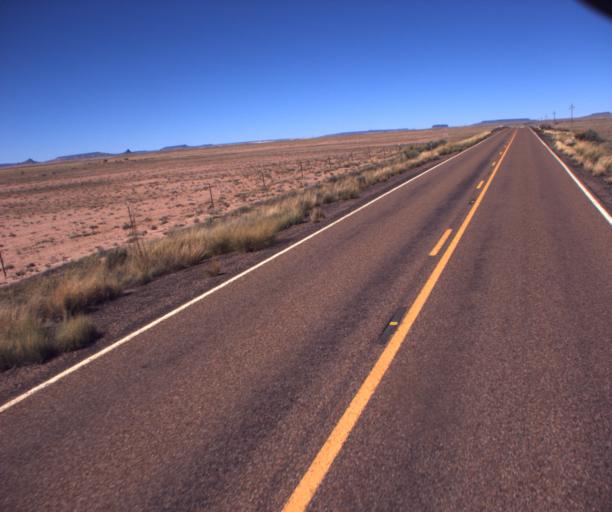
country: US
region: Arizona
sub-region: Navajo County
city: Holbrook
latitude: 35.0856
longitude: -110.0980
